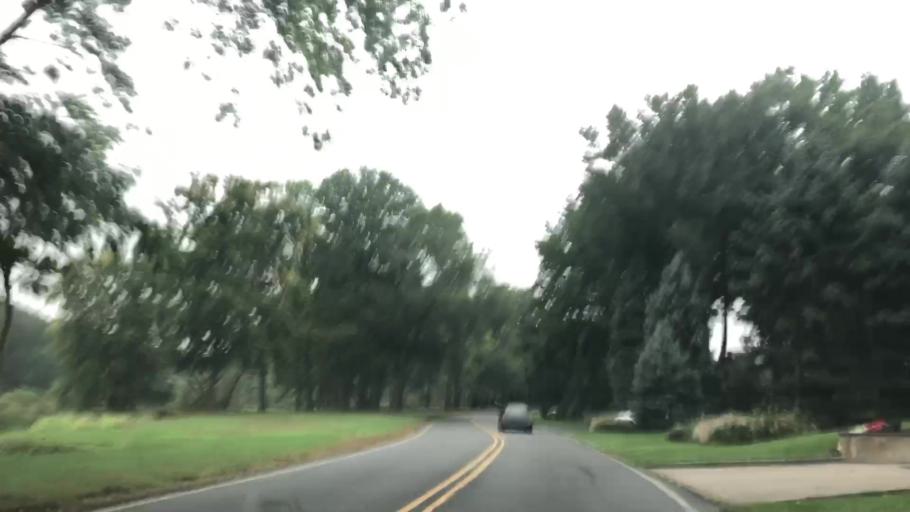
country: US
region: New Jersey
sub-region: Union County
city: Winfield
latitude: 40.6288
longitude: -74.2843
